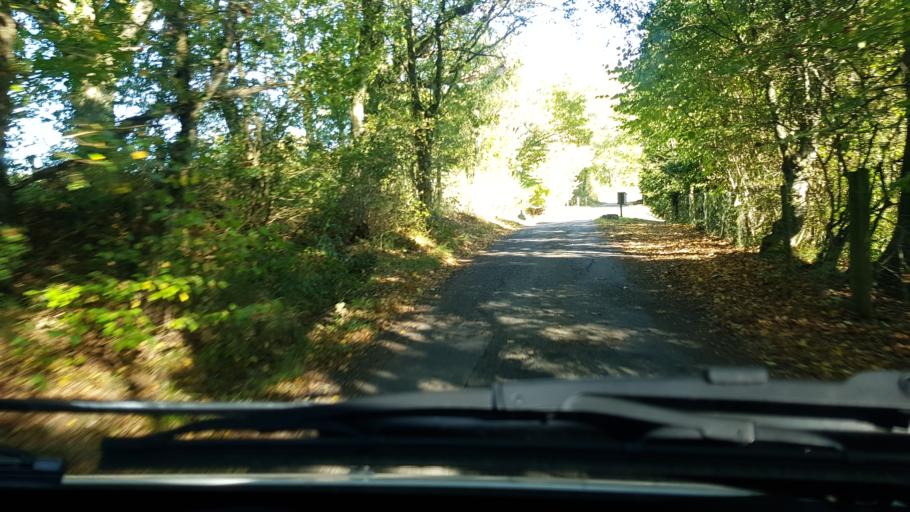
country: GB
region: England
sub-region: Surrey
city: Ockley
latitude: 51.1267
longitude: -0.3534
